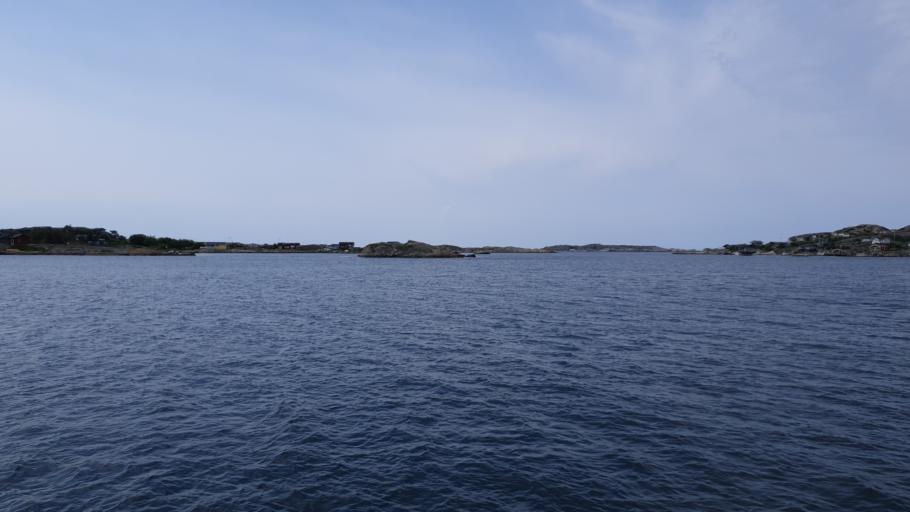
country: SE
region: Vaestra Goetaland
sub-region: Goteborg
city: Styrso
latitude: 57.5953
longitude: 11.7765
